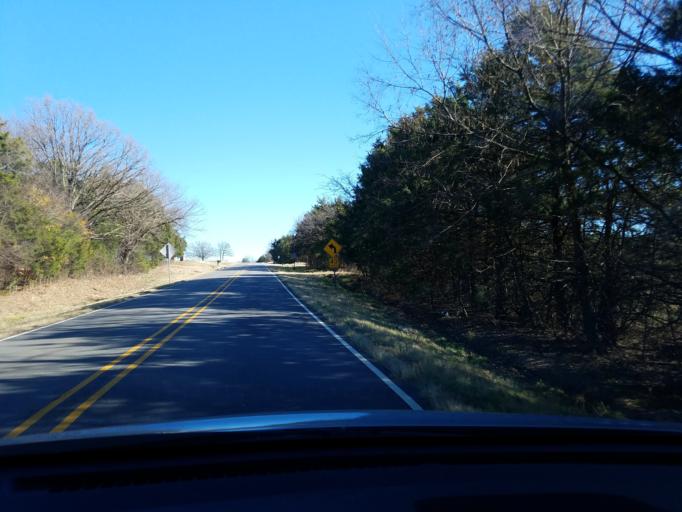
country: US
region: Arkansas
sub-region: Carroll County
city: Berryville
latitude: 36.4098
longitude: -93.5374
